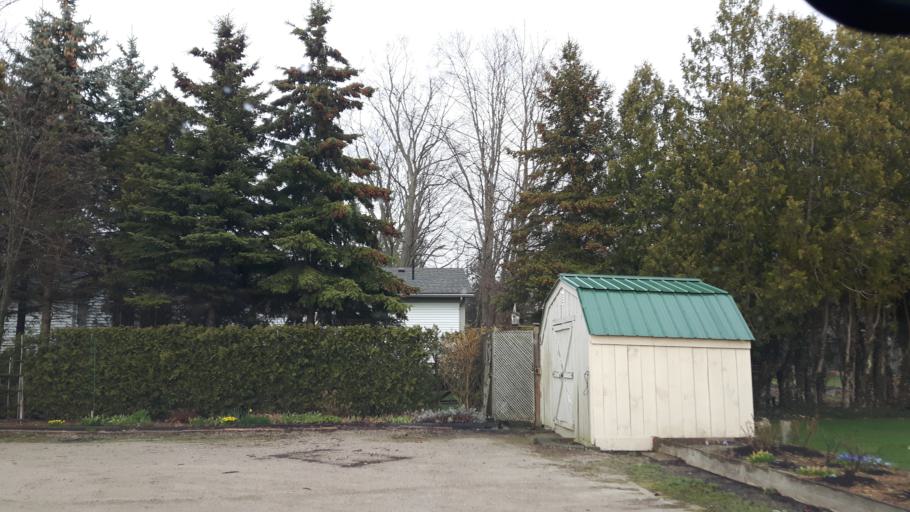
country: CA
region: Ontario
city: Bluewater
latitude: 43.5616
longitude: -81.6952
